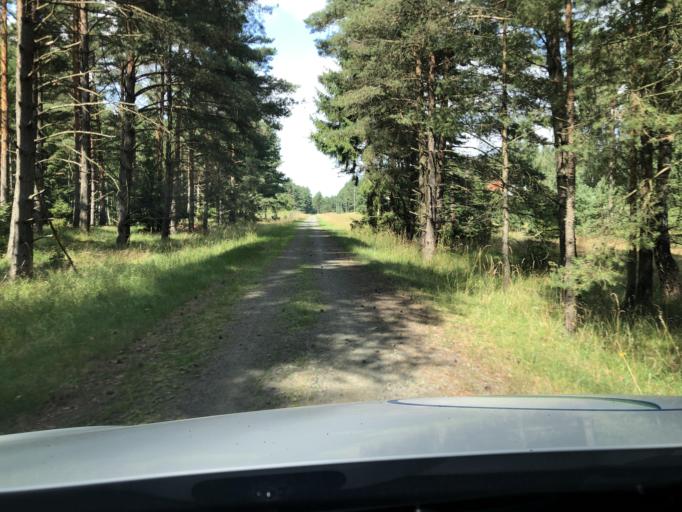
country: SE
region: Skane
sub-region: Kristianstads Kommun
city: Degeberga
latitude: 55.8653
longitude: 14.0812
